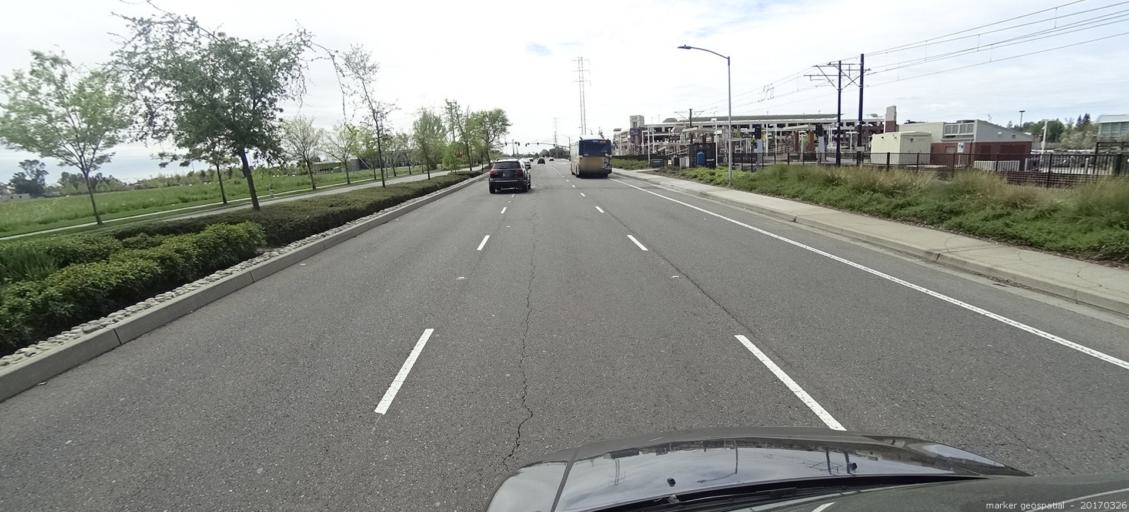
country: US
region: California
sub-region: Sacramento County
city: Laguna
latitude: 38.4548
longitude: -121.4180
